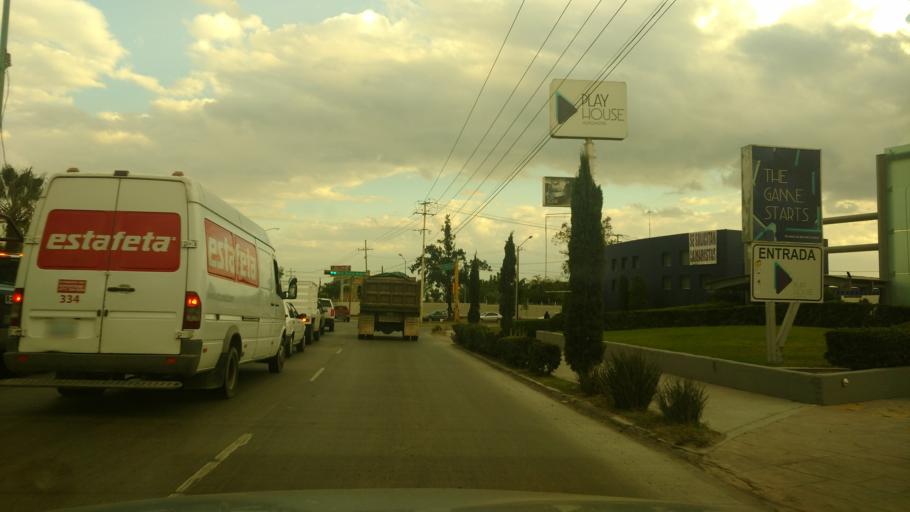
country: MX
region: Guanajuato
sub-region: Leon
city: Medina
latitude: 21.1586
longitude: -101.6441
